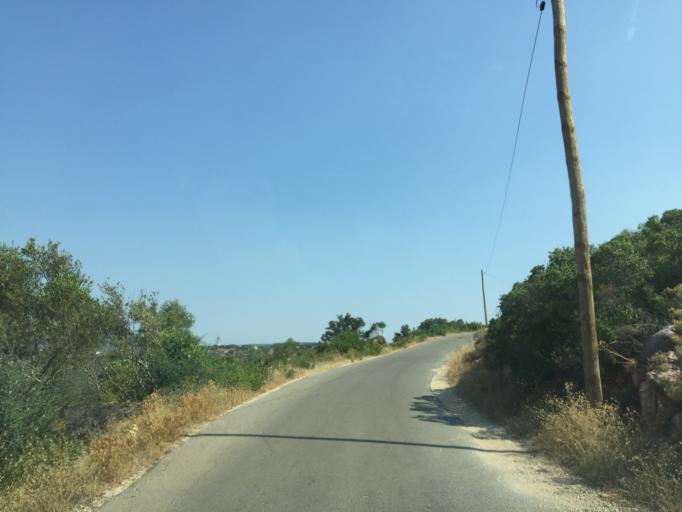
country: PT
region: Faro
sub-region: Loule
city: Loule
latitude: 37.1140
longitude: -8.0055
